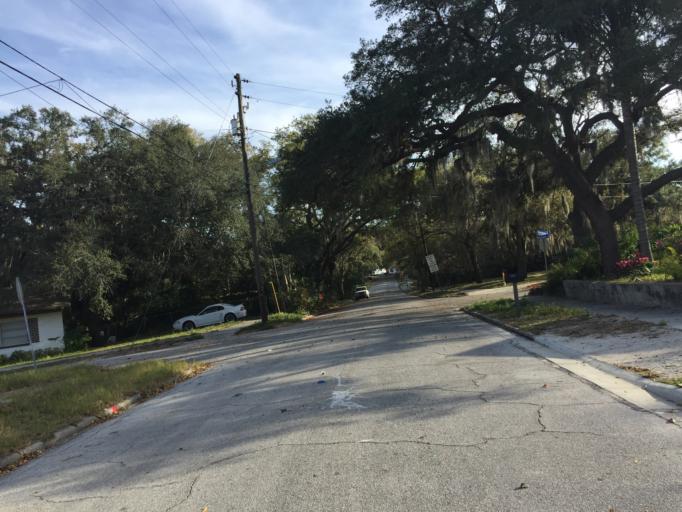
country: US
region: Florida
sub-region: Pinellas County
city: Clearwater
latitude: 27.9883
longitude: -82.7894
